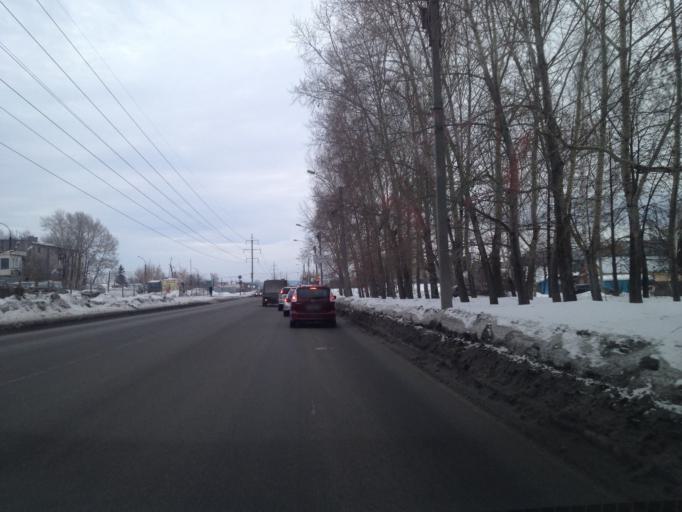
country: RU
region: Sverdlovsk
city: Sovkhoznyy
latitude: 56.7667
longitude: 60.5934
